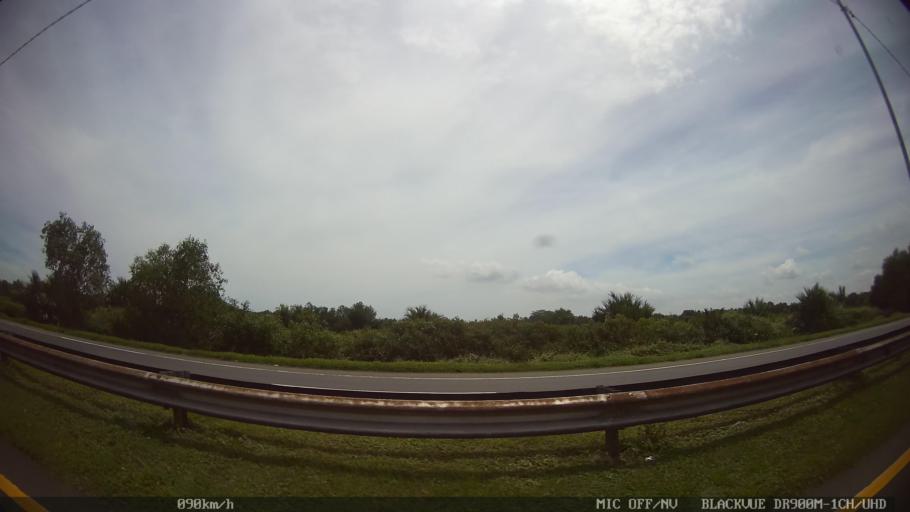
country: ID
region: North Sumatra
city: Labuhan Deli
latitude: 3.7343
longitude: 98.6803
